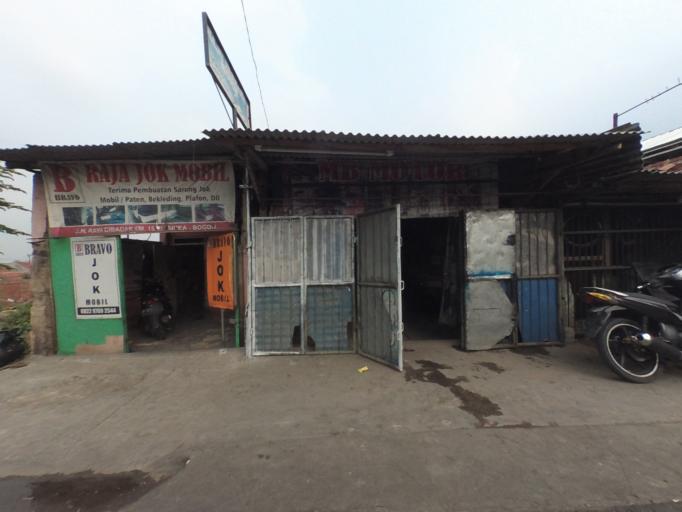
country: ID
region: West Java
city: Ciampea
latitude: -6.5600
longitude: 106.6858
